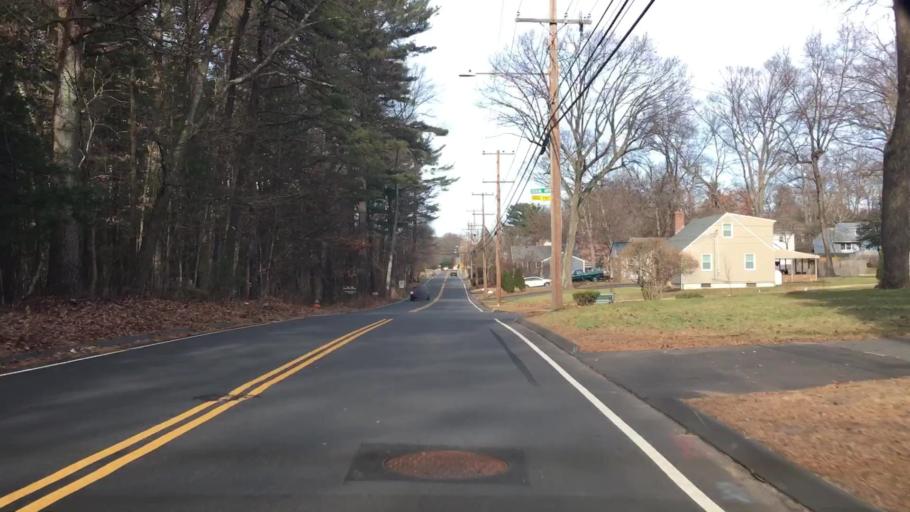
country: US
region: Connecticut
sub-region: Hartford County
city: Plainville
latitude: 41.6641
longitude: -72.9020
